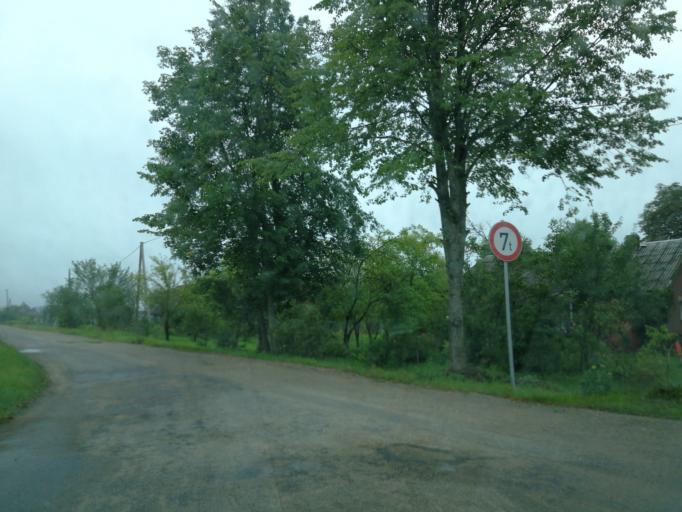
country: LV
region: Preilu Rajons
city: Jaunaglona
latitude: 56.3615
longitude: 27.0003
